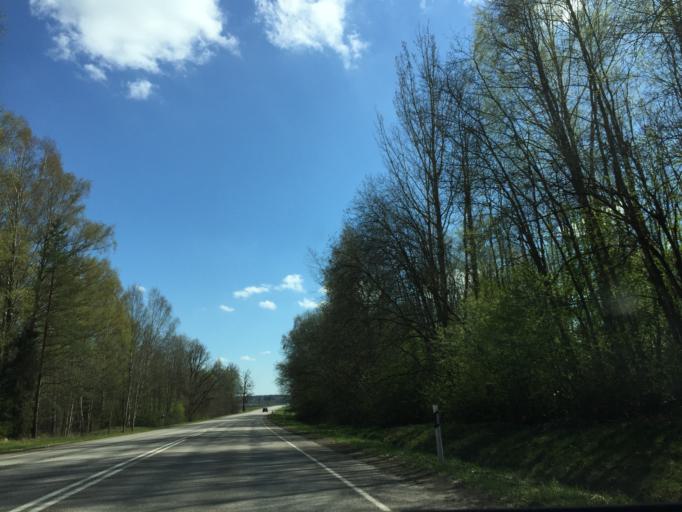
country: EE
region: Valgamaa
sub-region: Valga linn
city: Valga
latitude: 57.8860
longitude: 26.0583
